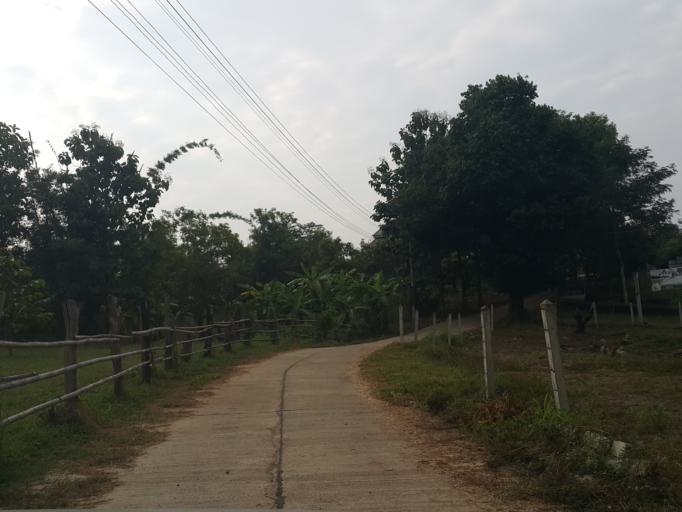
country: TH
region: Mae Hong Son
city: Wiang Nuea
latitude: 19.3725
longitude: 98.4468
